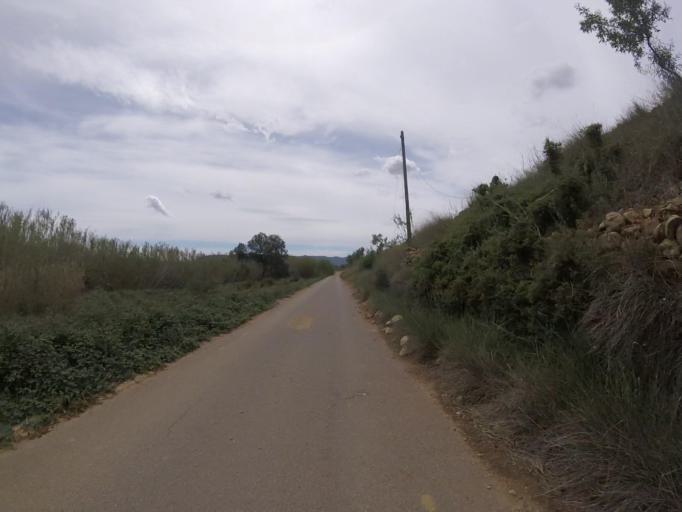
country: ES
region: Valencia
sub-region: Provincia de Castello
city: Benlloch
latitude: 40.1749
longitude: -0.0052
